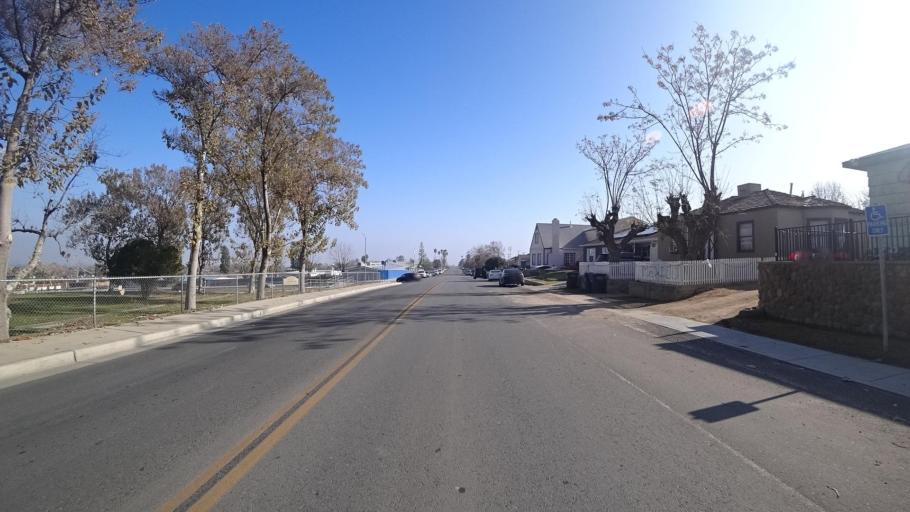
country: US
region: California
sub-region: Kern County
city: Taft Heights
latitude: 35.1367
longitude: -119.4749
